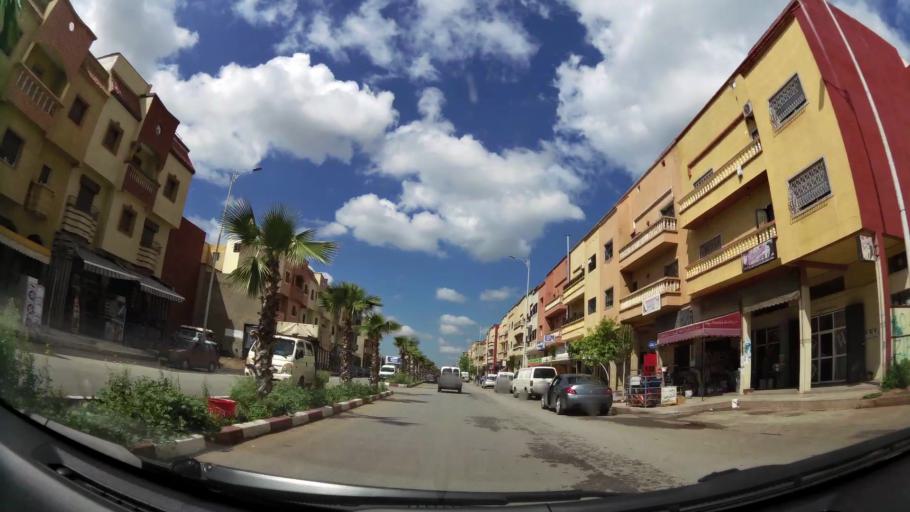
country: MA
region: Grand Casablanca
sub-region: Mediouna
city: Mediouna
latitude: 33.3754
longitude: -7.5368
